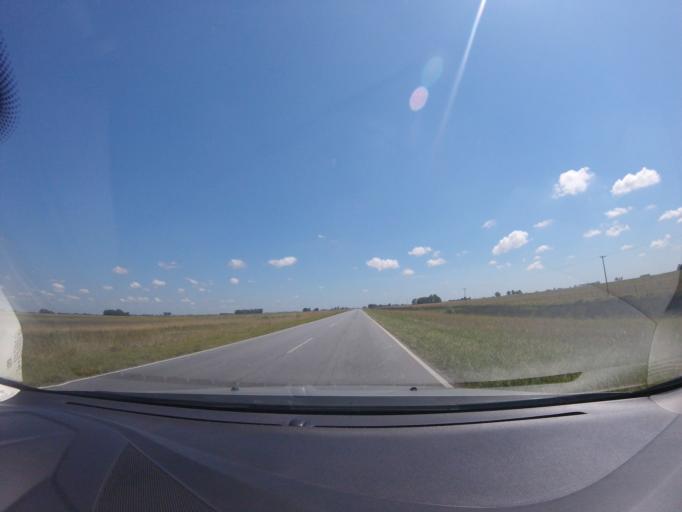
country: AR
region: Buenos Aires
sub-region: Partido de Rauch
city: Rauch
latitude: -36.9028
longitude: -58.9885
